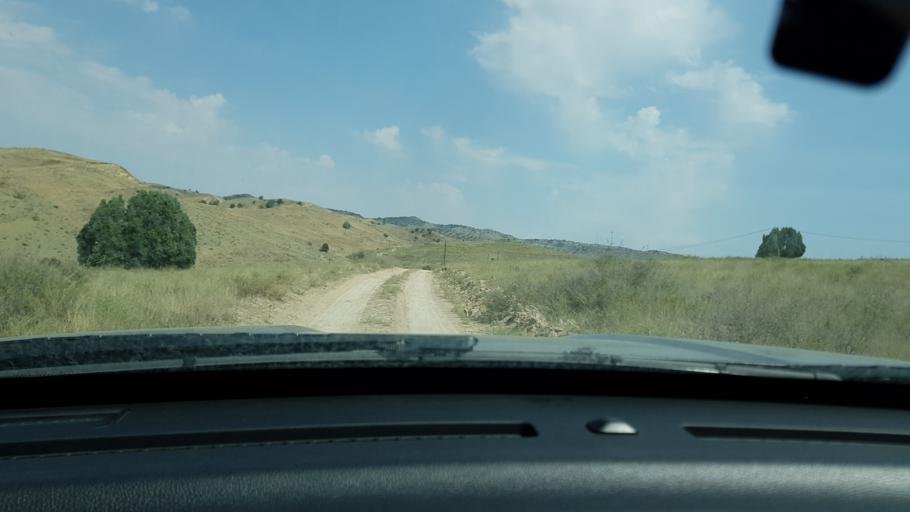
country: TM
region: Ahal
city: Baharly
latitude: 38.4116
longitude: 56.9246
